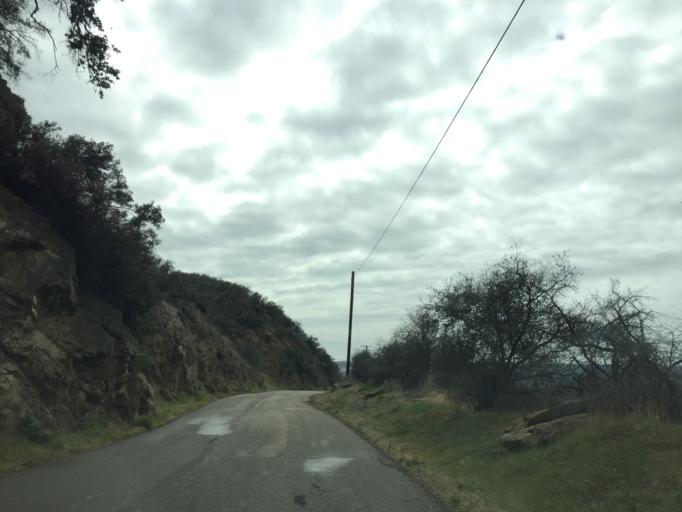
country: US
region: California
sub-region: Santa Barbara County
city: Goleta
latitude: 34.4873
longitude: -119.7967
